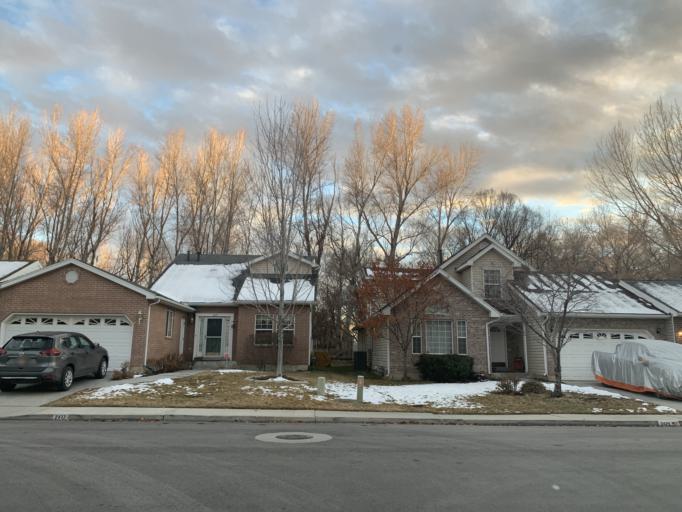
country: US
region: Utah
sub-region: Utah County
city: Provo
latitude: 40.2384
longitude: -111.7012
